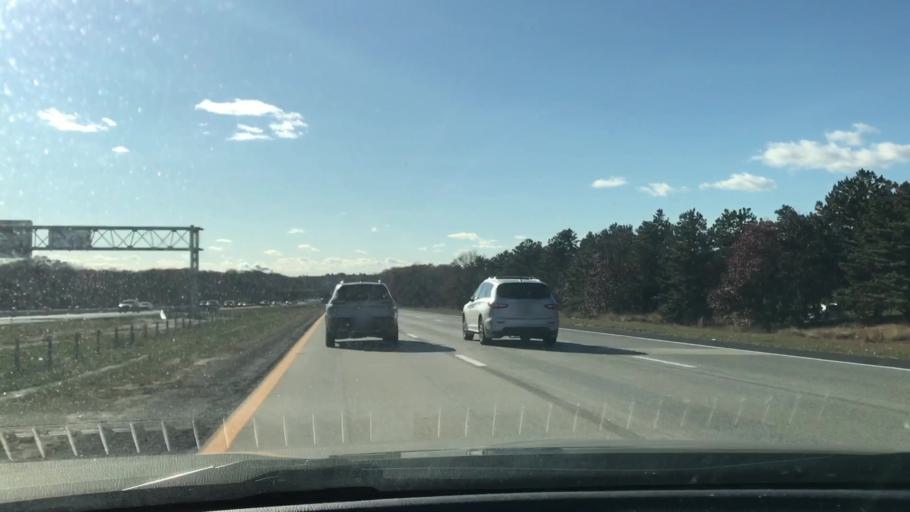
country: US
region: New York
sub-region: Suffolk County
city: Yaphank
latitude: 40.8395
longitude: -72.8997
